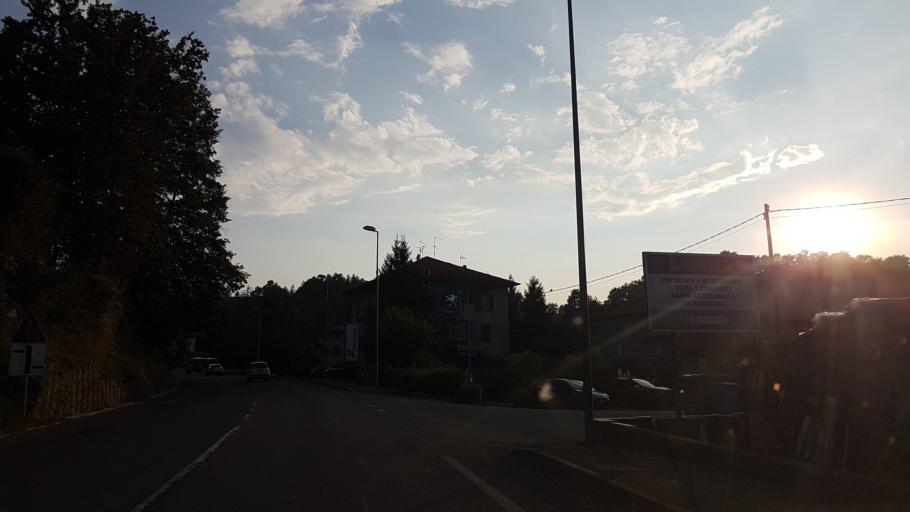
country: IT
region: Emilia-Romagna
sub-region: Provincia di Parma
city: Albareto
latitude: 44.4697
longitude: 9.7328
